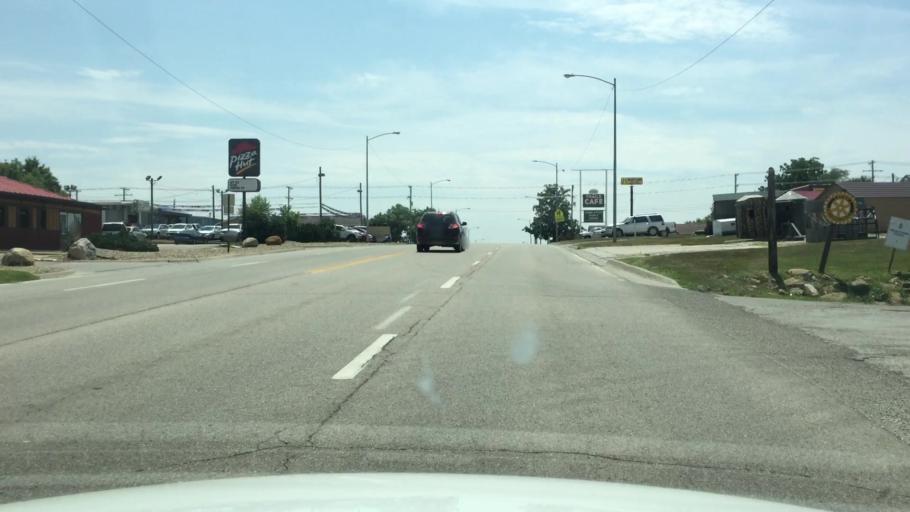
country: US
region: Kansas
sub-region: Jackson County
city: Holton
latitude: 39.4677
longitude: -95.7479
